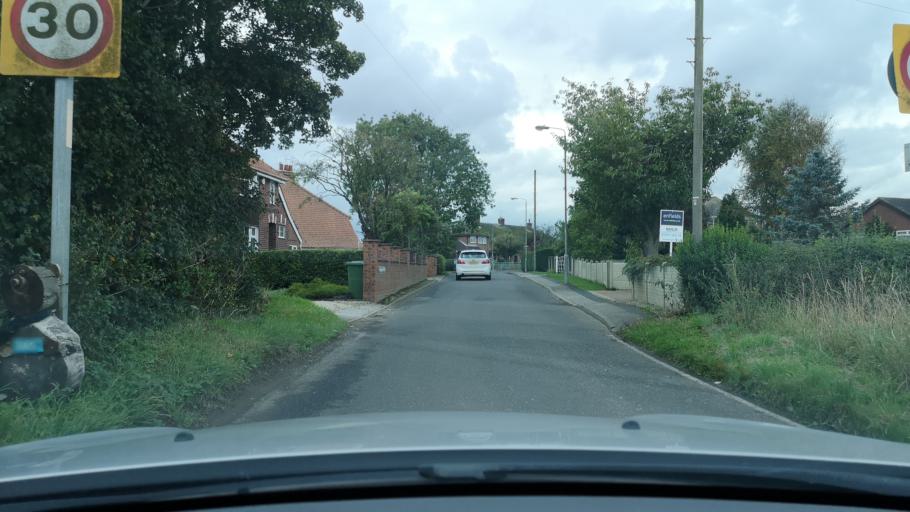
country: GB
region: England
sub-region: City and Borough of Wakefield
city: Darrington
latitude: 53.6630
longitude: -1.2954
